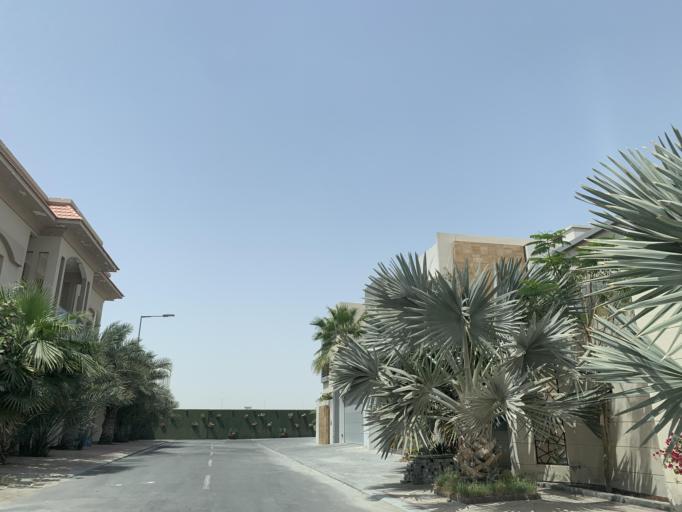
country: BH
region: Northern
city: Madinat `Isa
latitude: 26.1643
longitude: 50.5220
